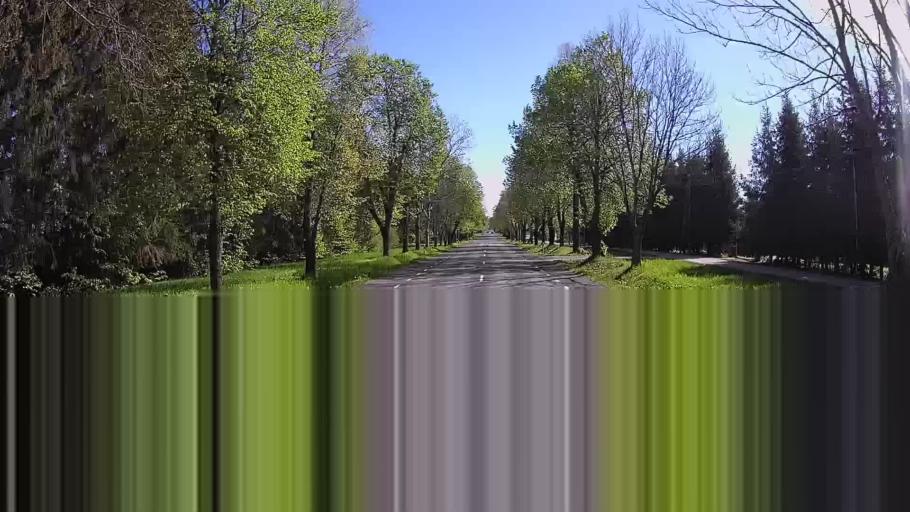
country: EE
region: Polvamaa
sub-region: Raepina vald
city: Rapina
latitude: 58.0970
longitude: 27.4349
